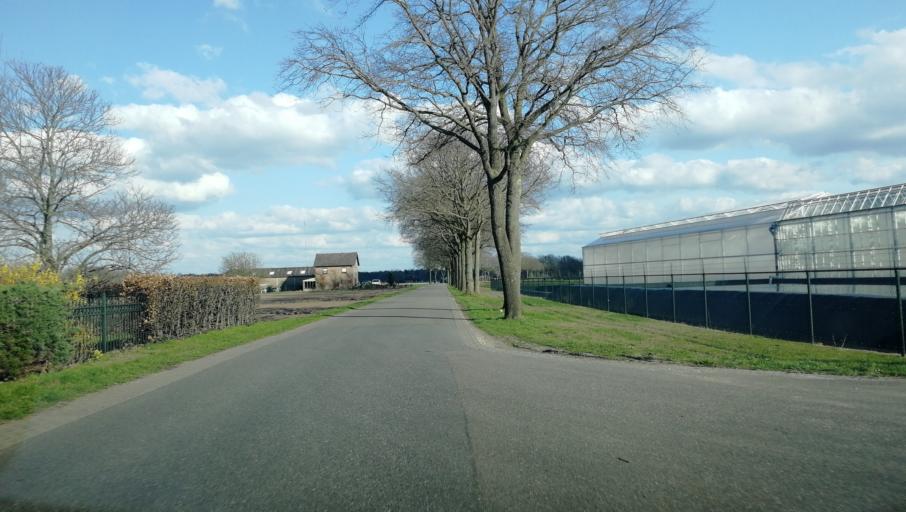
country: NL
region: Limburg
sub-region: Gemeente Venlo
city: Arcen
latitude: 51.4357
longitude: 6.1081
